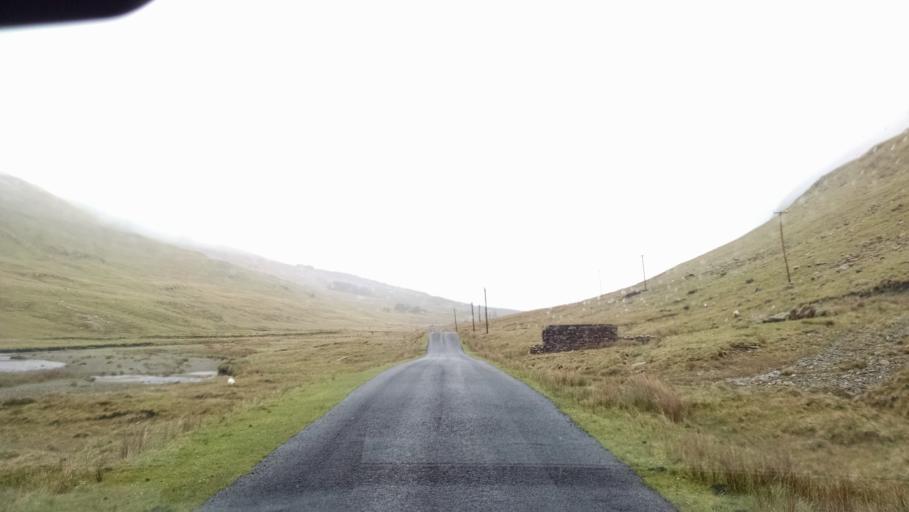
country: IE
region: Connaught
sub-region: Maigh Eo
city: Westport
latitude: 53.6457
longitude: -9.7299
